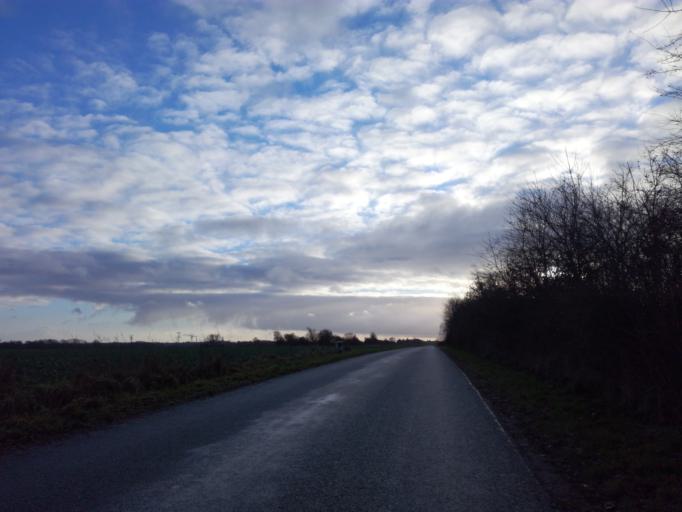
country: DK
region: South Denmark
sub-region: Fredericia Kommune
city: Taulov
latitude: 55.5665
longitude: 9.6045
